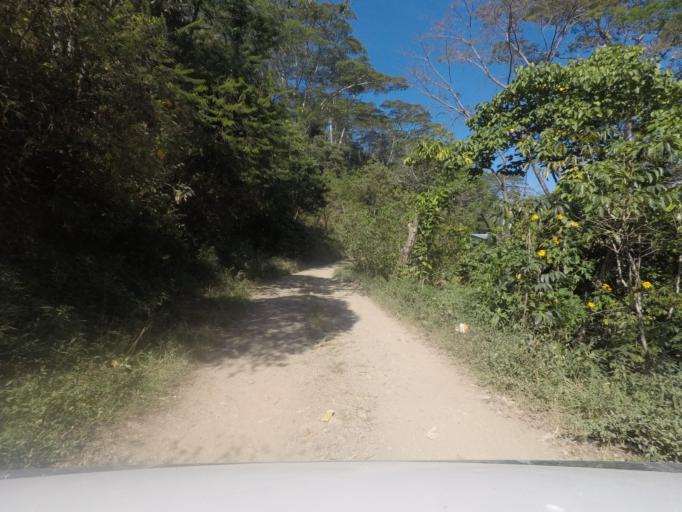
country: TL
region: Ermera
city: Gleno
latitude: -8.7230
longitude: 125.3313
